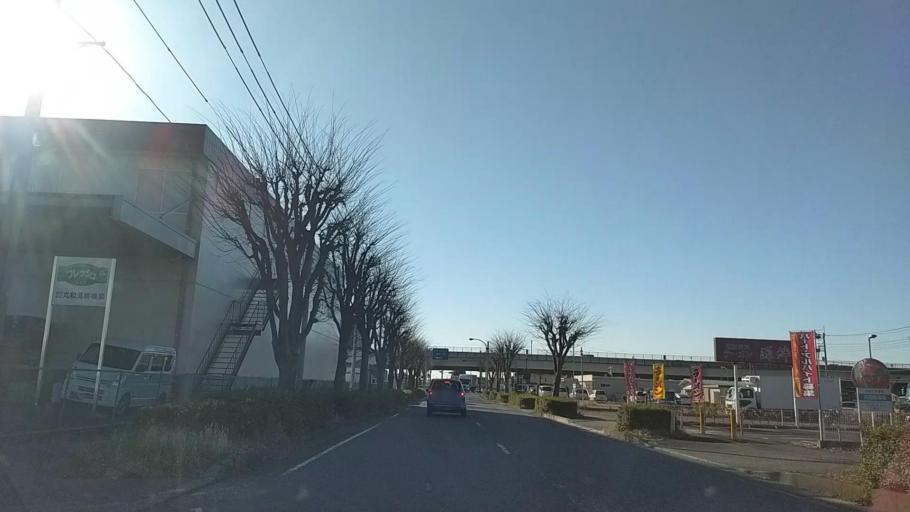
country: JP
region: Kanagawa
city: Atsugi
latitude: 35.4206
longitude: 139.3554
